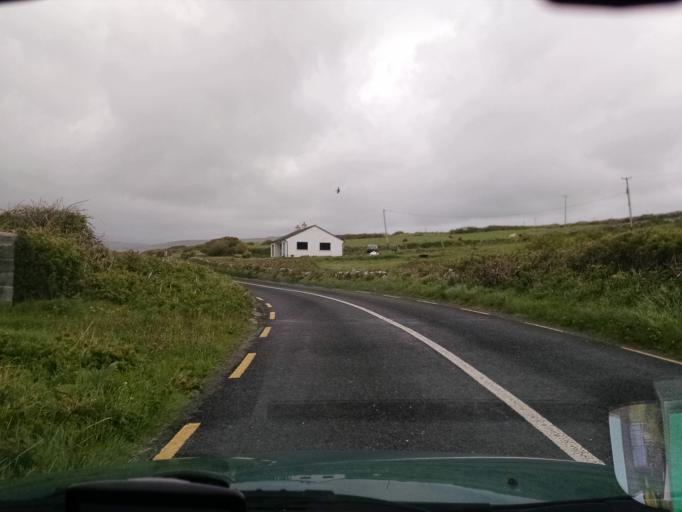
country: IE
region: Connaught
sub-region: County Galway
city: Bearna
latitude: 53.0822
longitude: -9.3310
